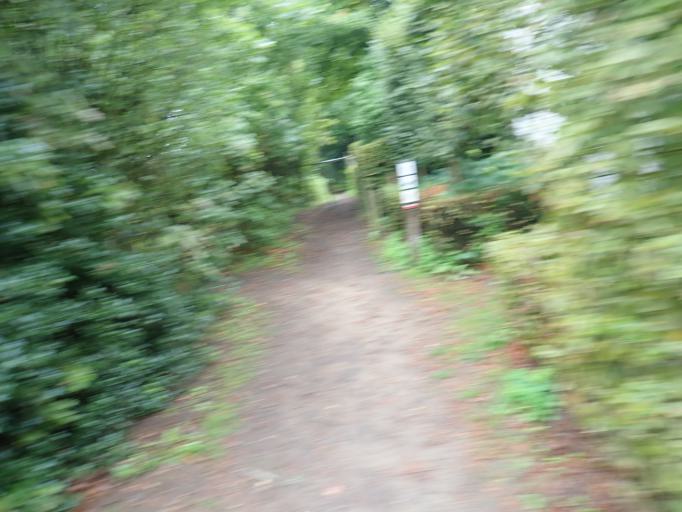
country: BE
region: Flanders
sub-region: Provincie Antwerpen
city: Zandhoven
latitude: 51.2437
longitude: 4.6761
